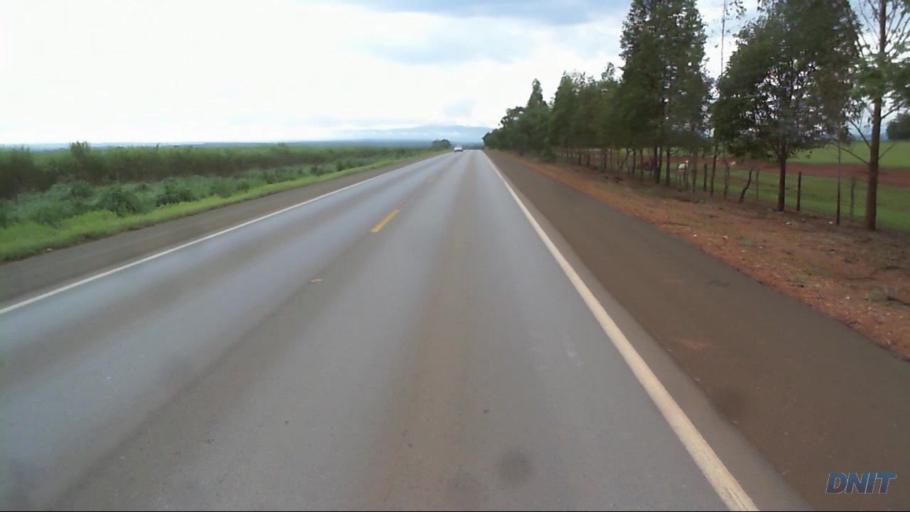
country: BR
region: Goias
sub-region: Uruacu
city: Uruacu
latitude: -14.7133
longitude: -49.1070
